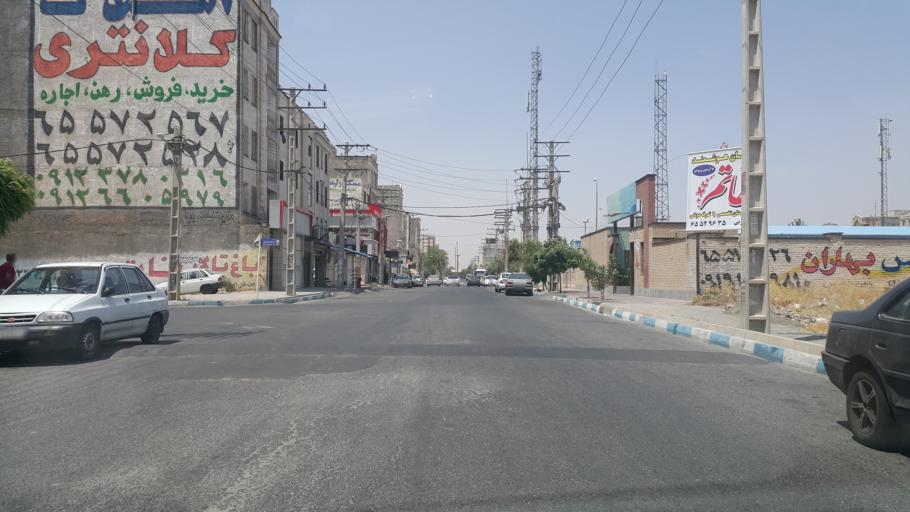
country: IR
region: Tehran
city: Shahre Jadide Andisheh
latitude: 35.6648
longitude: 51.0111
